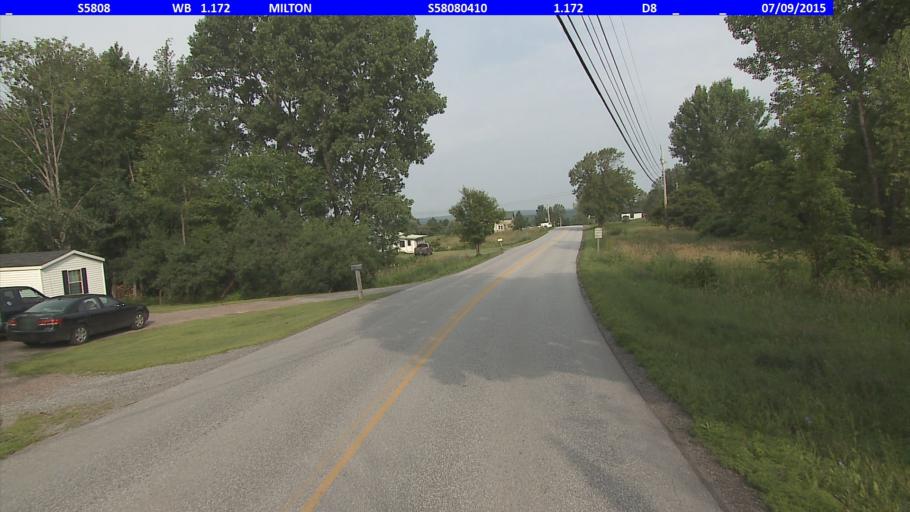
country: US
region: Vermont
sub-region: Chittenden County
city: Milton
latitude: 44.6355
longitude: -73.0912
